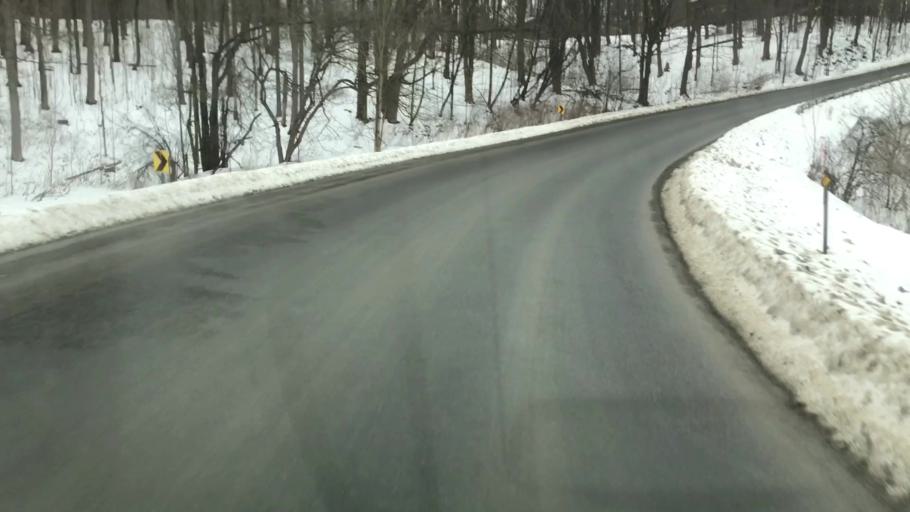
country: US
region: New York
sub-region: Cortland County
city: Cortland West
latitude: 42.6529
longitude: -76.2722
